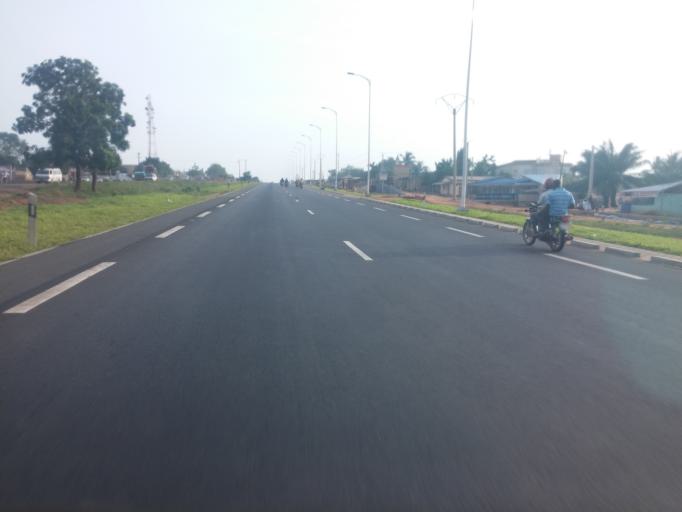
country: TG
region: Maritime
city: Tsevie
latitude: 6.3162
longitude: 1.2171
